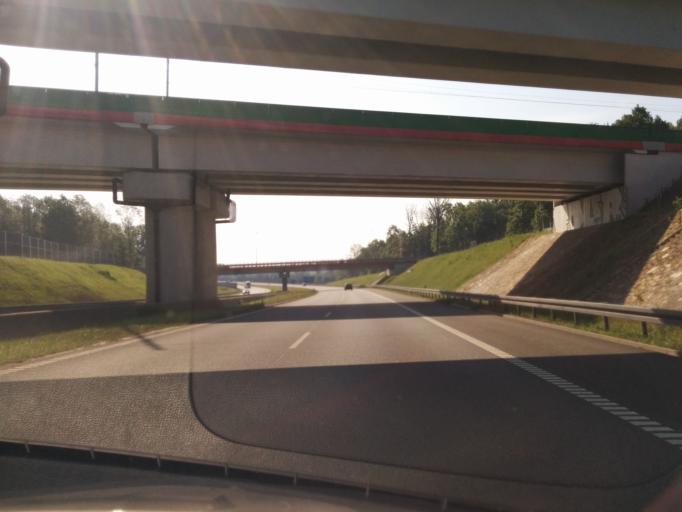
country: PL
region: Silesian Voivodeship
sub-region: Powiat tarnogorski
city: Radzionkow
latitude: 50.3751
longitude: 18.8782
